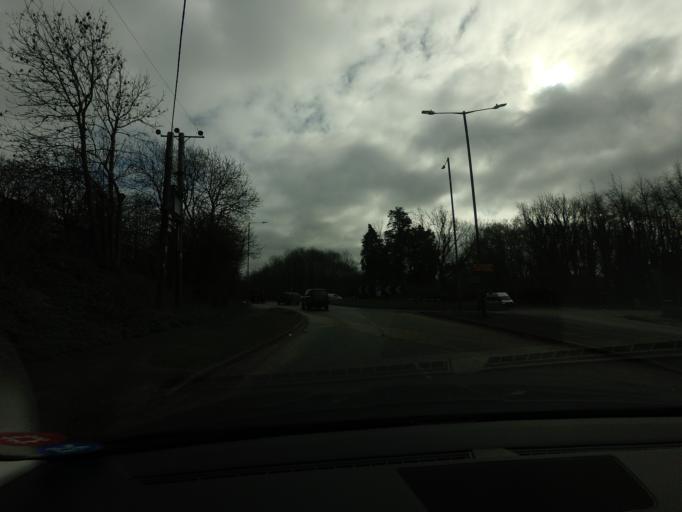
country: GB
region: England
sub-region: Kent
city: Eynsford
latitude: 51.3834
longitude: 0.2216
